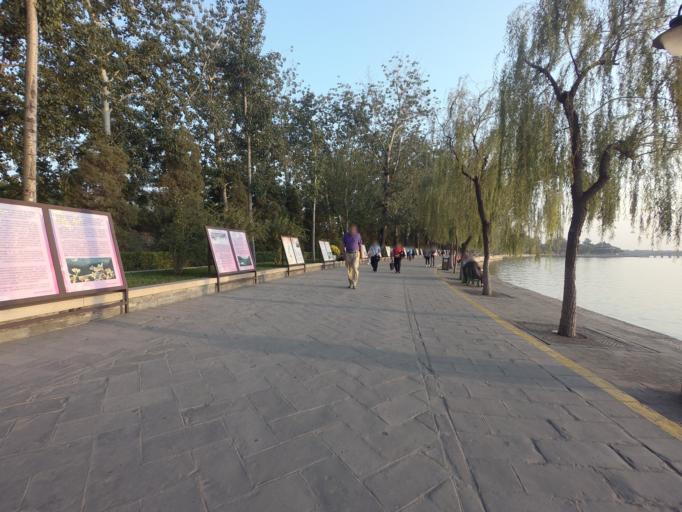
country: CN
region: Beijing
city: Haidian
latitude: 39.9932
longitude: 116.2744
